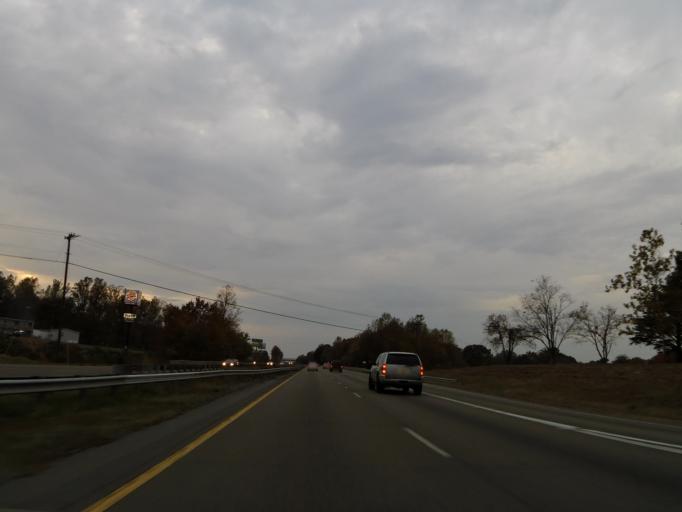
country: US
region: North Carolina
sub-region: Burke County
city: Icard
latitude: 35.7200
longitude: -81.4669
